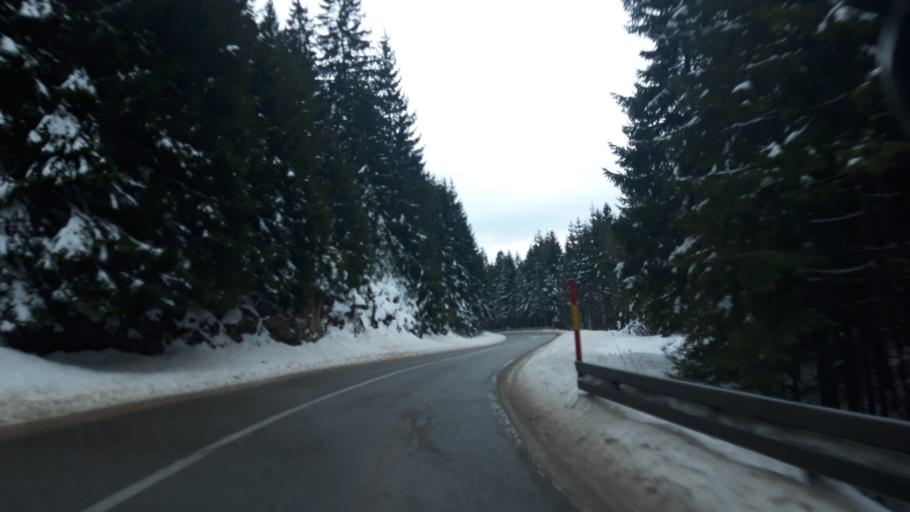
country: BA
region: Republika Srpska
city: Han Pijesak
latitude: 44.1181
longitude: 18.9700
